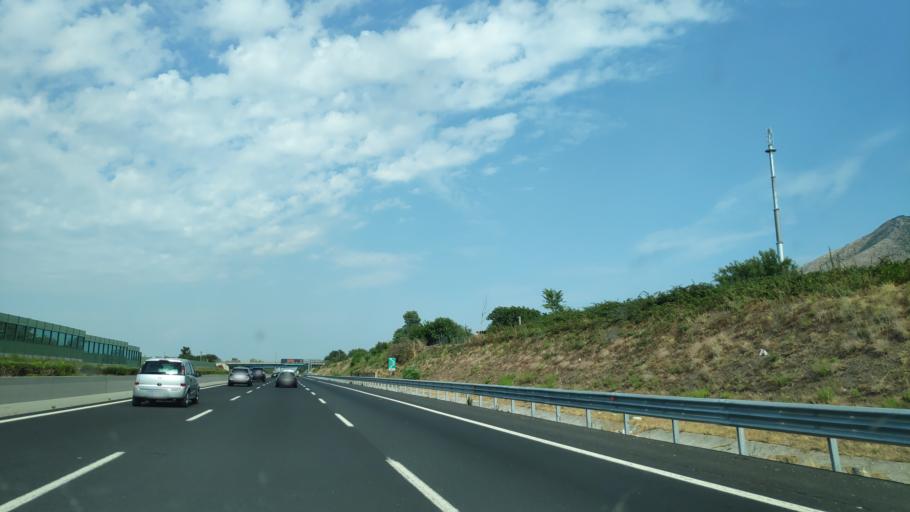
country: IT
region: Campania
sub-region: Provincia di Caserta
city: San Prisco
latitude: 41.0902
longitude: 14.2821
